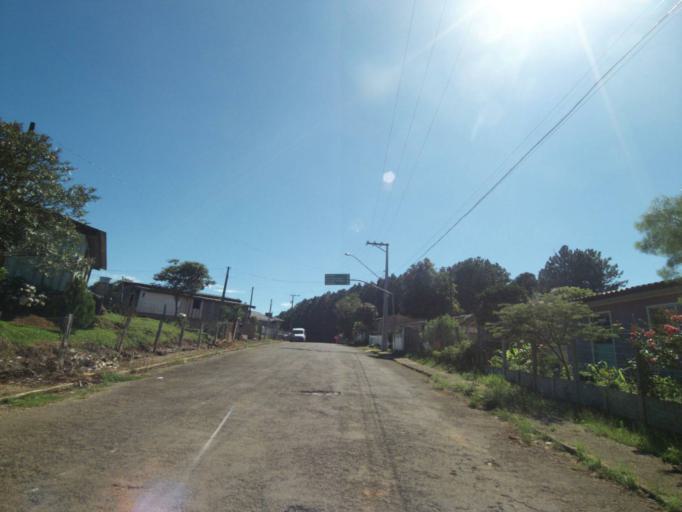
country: BR
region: Parana
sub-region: Pinhao
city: Pinhao
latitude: -25.8354
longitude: -52.0237
